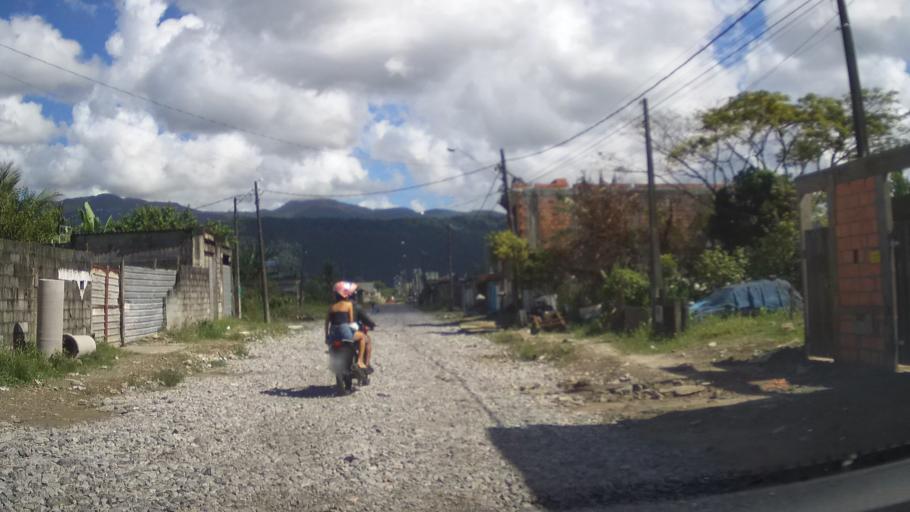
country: BR
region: Sao Paulo
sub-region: Praia Grande
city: Praia Grande
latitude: -24.0207
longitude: -46.5174
